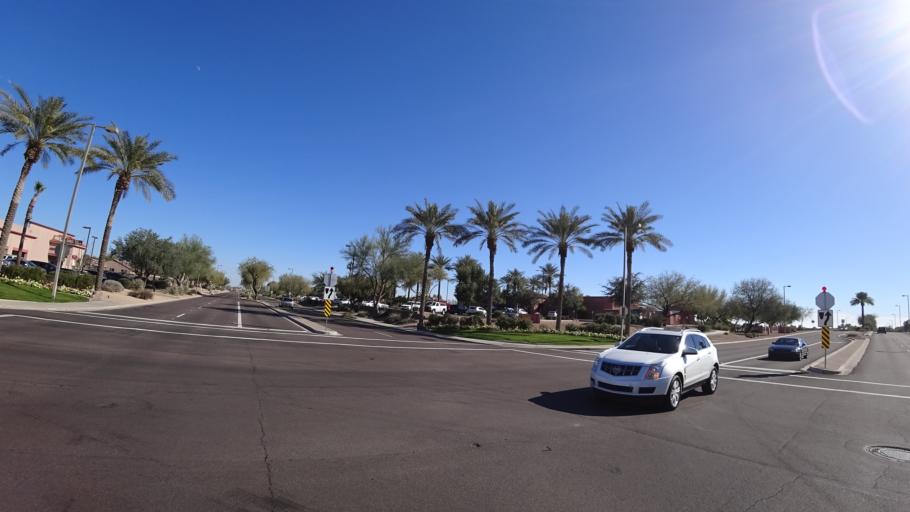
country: US
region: Arizona
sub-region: Maricopa County
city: Sun City West
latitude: 33.6547
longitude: -112.4046
